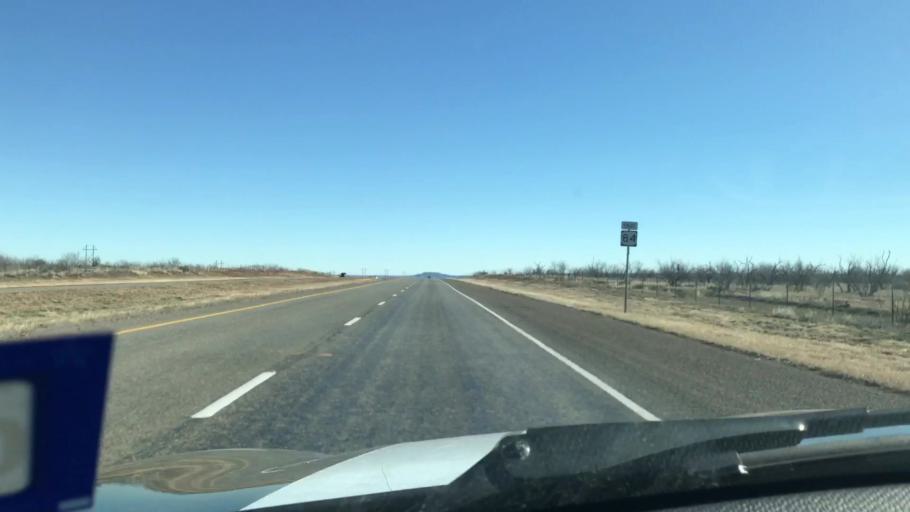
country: US
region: Texas
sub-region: Garza County
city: Post
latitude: 33.0993
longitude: -101.2570
